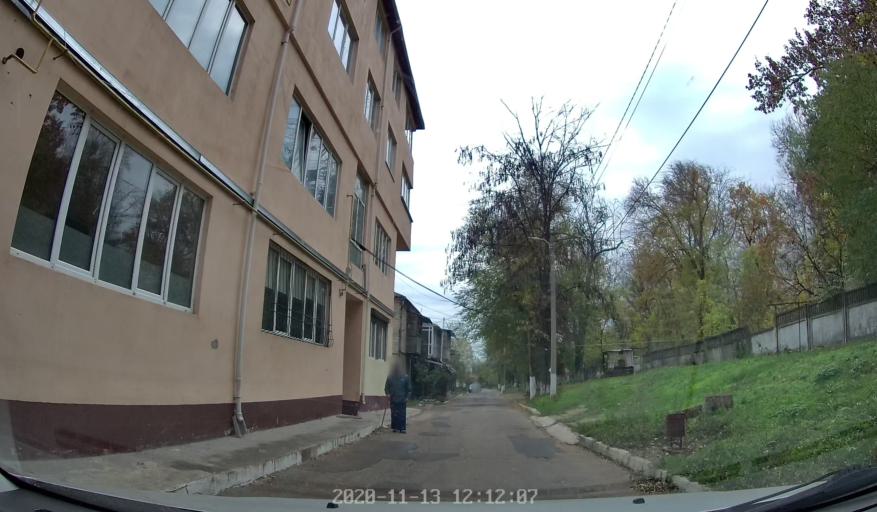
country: MD
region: Chisinau
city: Chisinau
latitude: 46.9561
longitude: 28.8359
